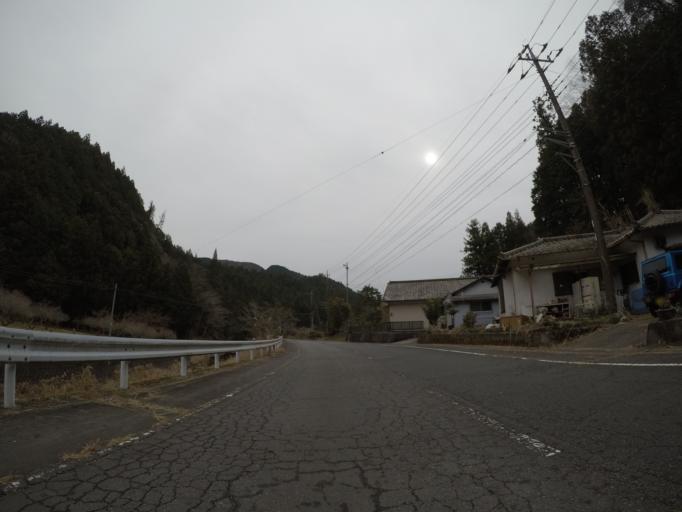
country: JP
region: Shizuoka
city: Fujinomiya
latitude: 35.2726
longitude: 138.5294
